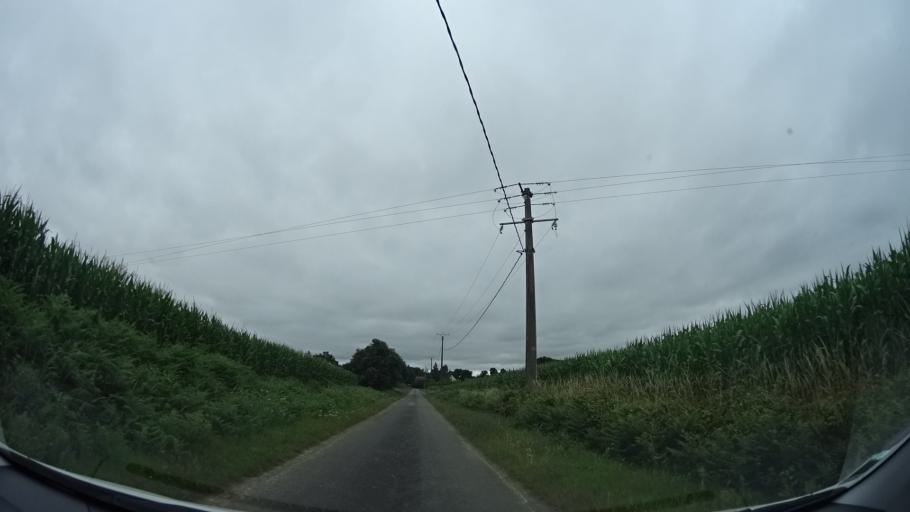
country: FR
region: Brittany
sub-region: Departement des Cotes-d'Armor
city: Evran
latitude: 48.3376
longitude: -1.9492
